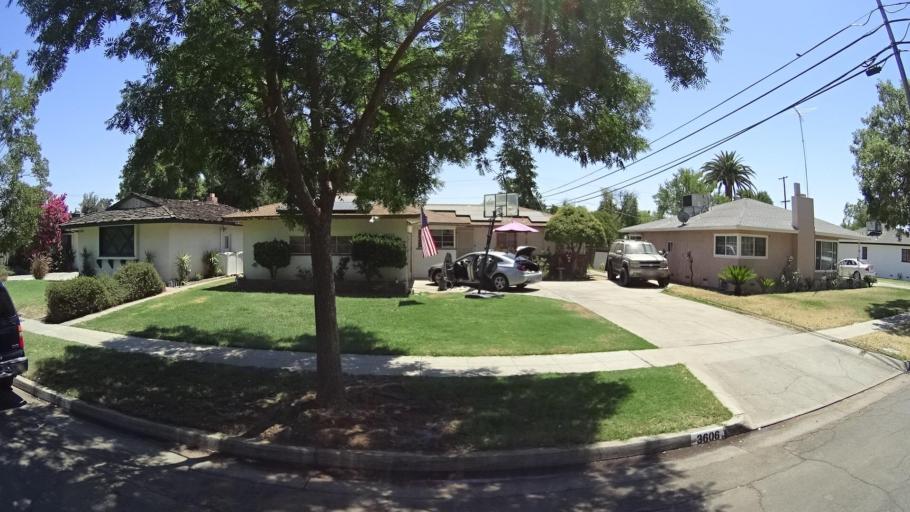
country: US
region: California
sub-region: Fresno County
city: Fresno
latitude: 36.7833
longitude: -119.7787
